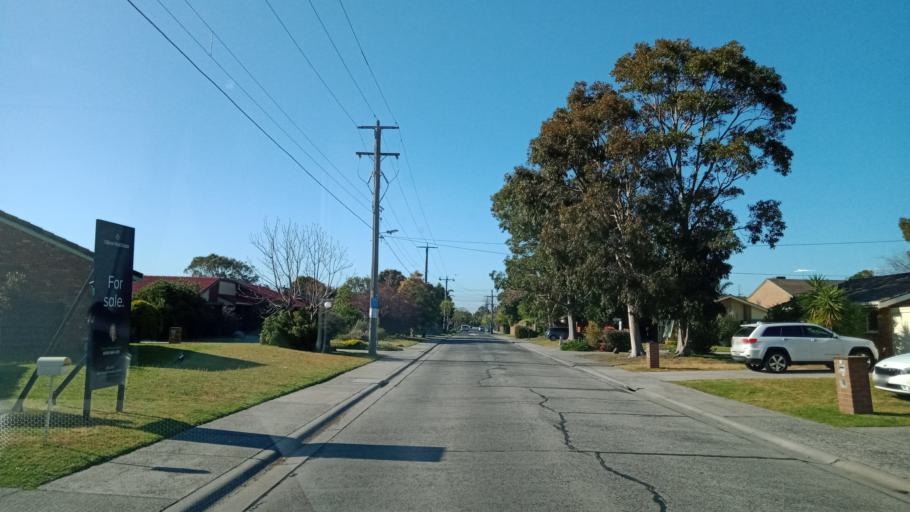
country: AU
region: Victoria
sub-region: Kingston
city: Chelsea
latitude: -38.0451
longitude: 145.1225
